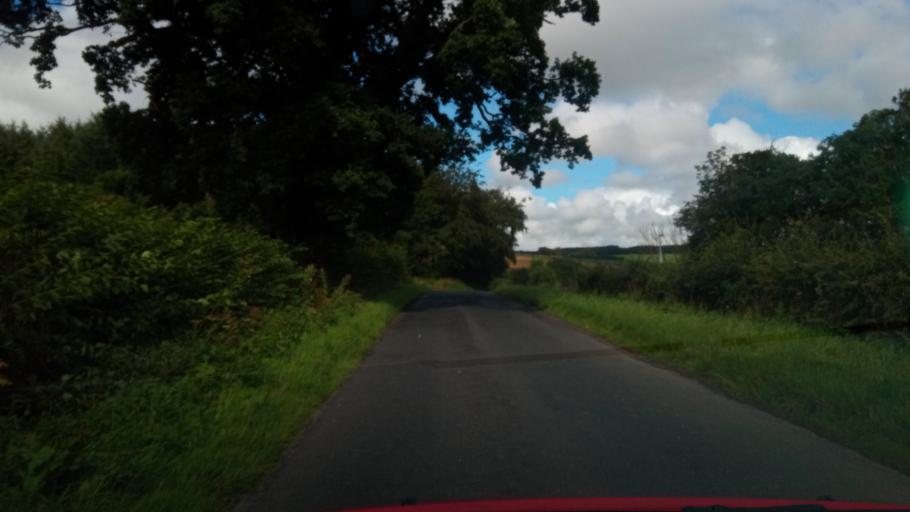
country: GB
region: Scotland
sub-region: The Scottish Borders
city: Earlston
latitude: 55.6400
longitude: -2.6984
